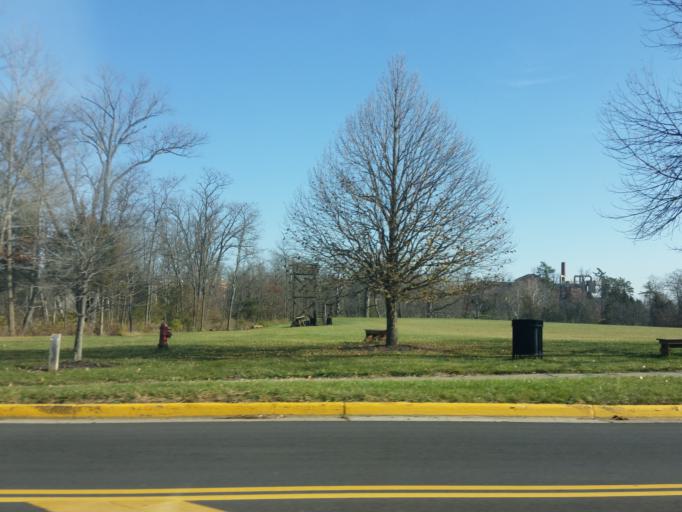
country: US
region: Ohio
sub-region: Butler County
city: Oxford
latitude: 39.5028
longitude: -84.7307
